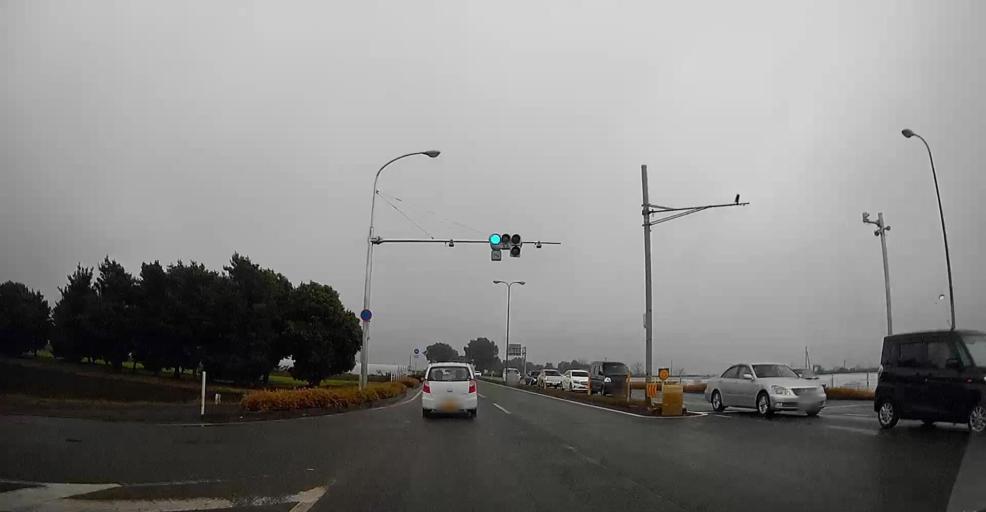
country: JP
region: Kumamoto
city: Ozu
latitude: 32.8291
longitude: 130.8580
